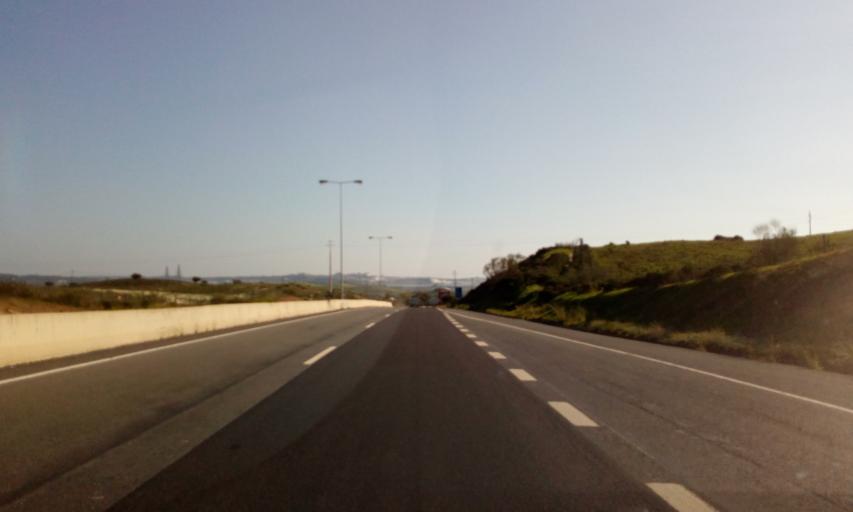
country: PT
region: Faro
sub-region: Castro Marim
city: Castro Marim
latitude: 37.2412
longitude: -7.4528
